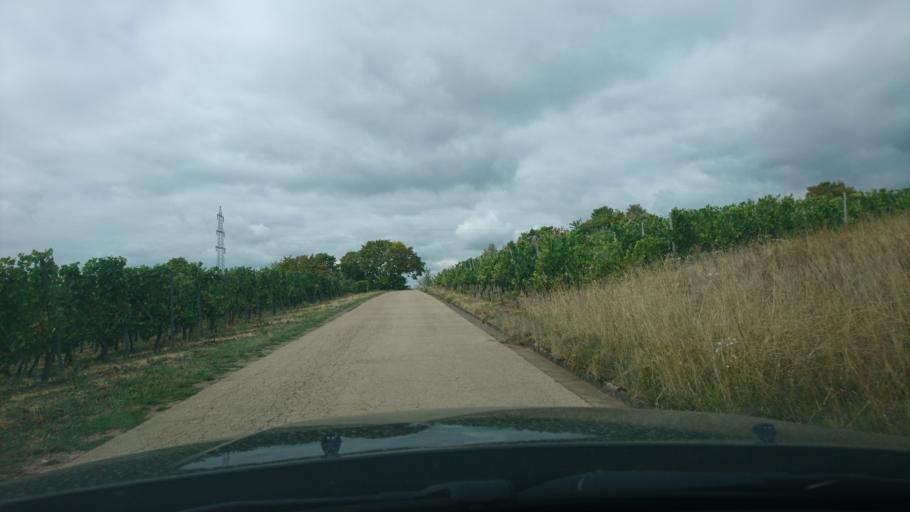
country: DE
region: Rheinland-Pfalz
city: Wiltingen
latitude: 49.6699
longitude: 6.6012
